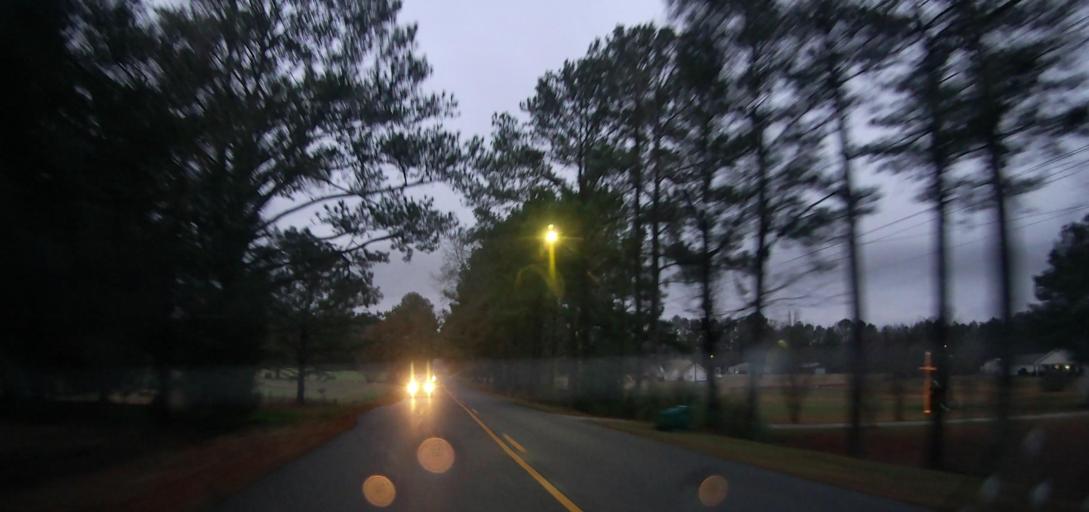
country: US
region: Alabama
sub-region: Tuscaloosa County
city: Vance
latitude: 33.1413
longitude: -87.2298
